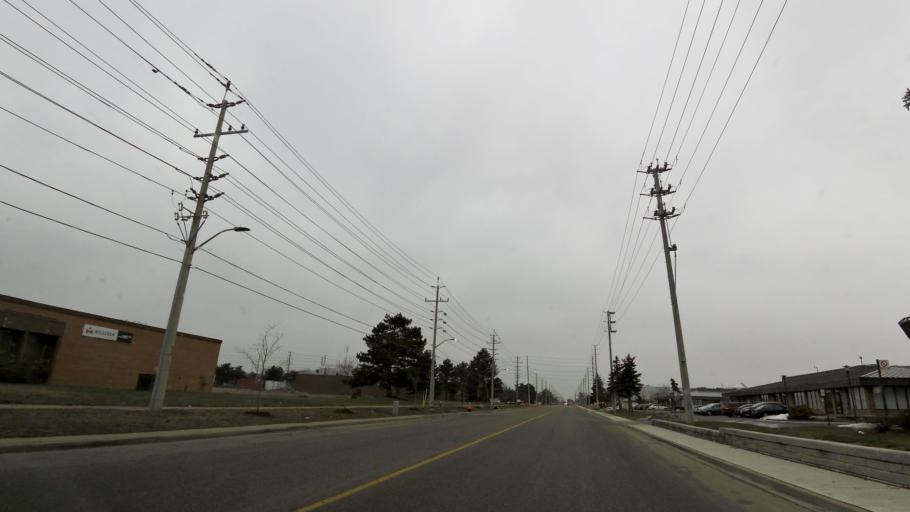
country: CA
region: Ontario
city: Etobicoke
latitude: 43.6983
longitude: -79.6117
